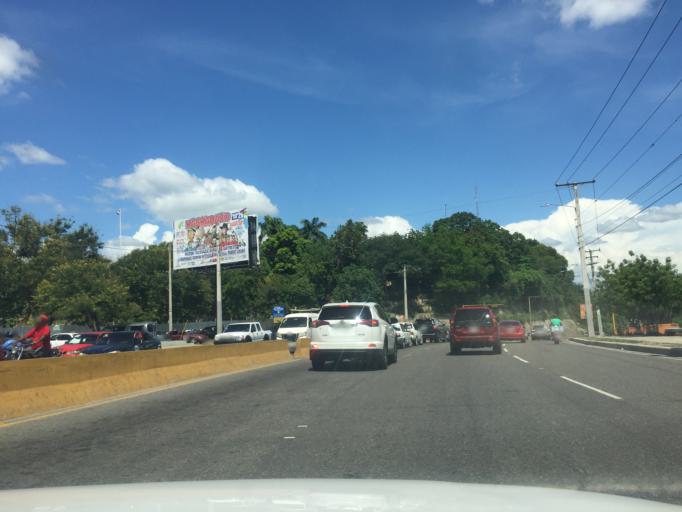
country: DO
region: Santiago
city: Santiago de los Caballeros
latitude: 19.4489
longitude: -70.7046
